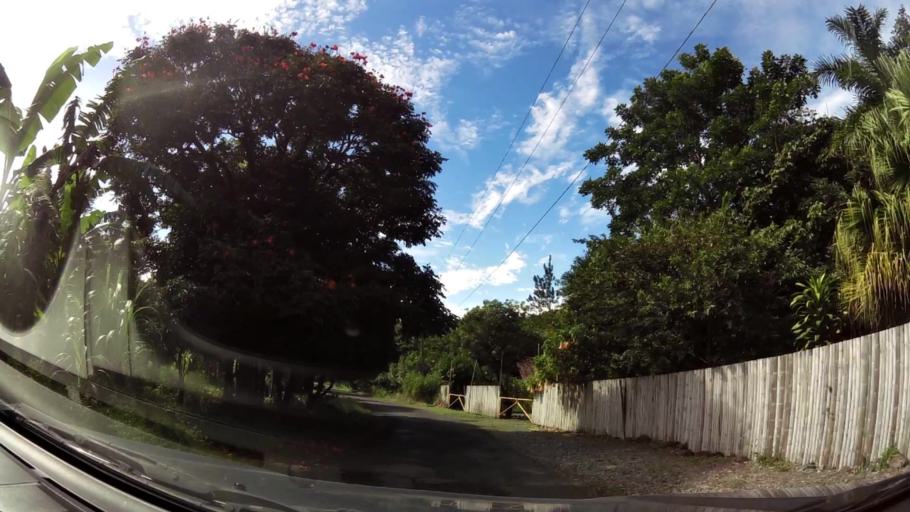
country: PA
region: Chiriqui
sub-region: Distrito Boquete
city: Boquete
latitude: 8.7712
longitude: -82.4339
